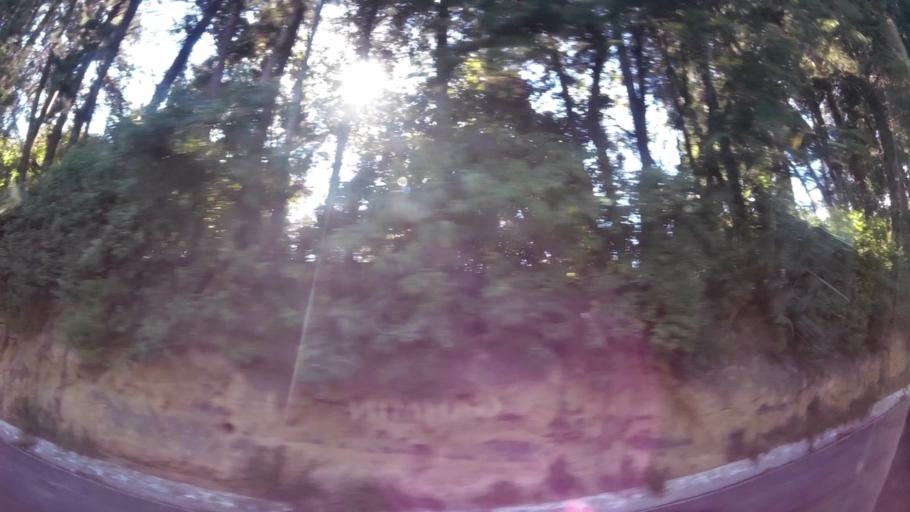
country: GT
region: Sacatepequez
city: Santa Lucia Milpas Altas
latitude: 14.5709
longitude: -90.6404
